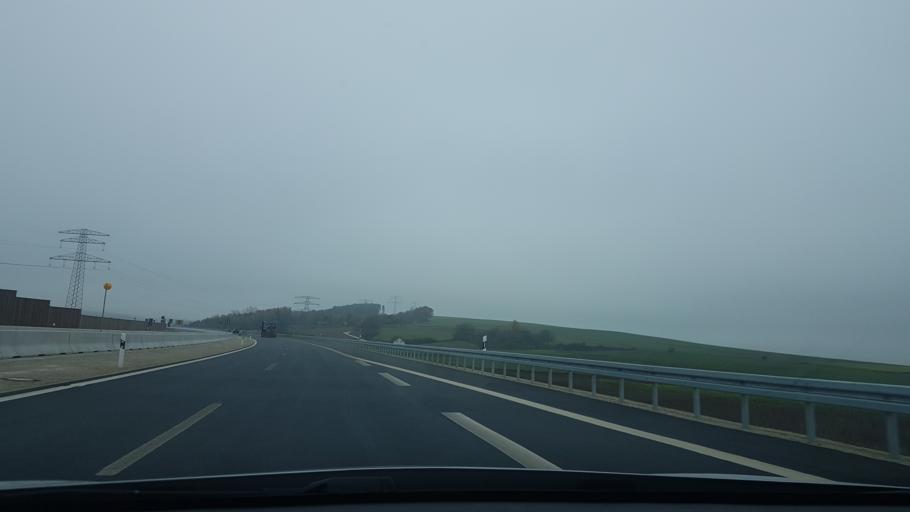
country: DE
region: Bavaria
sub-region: Lower Bavaria
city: Essenbach
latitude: 48.6195
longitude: 12.2284
